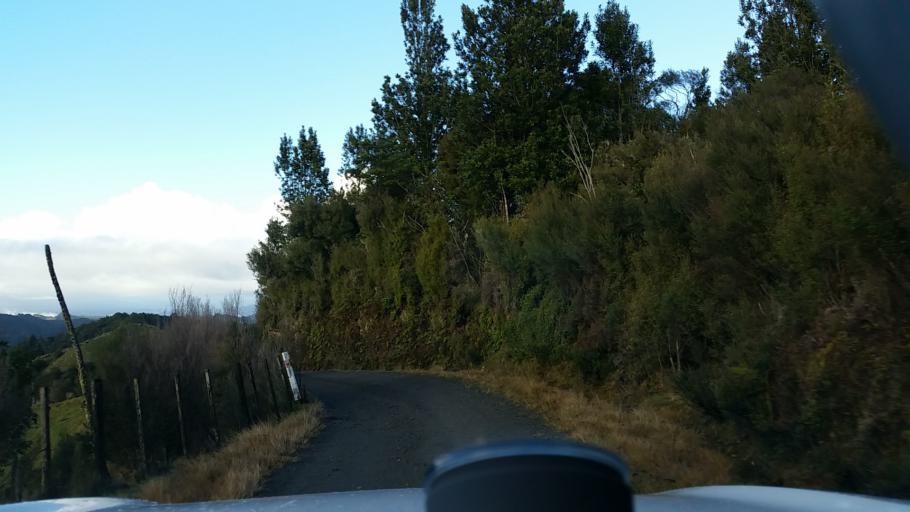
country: NZ
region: Taranaki
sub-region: South Taranaki District
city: Eltham
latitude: -39.4207
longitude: 174.5568
